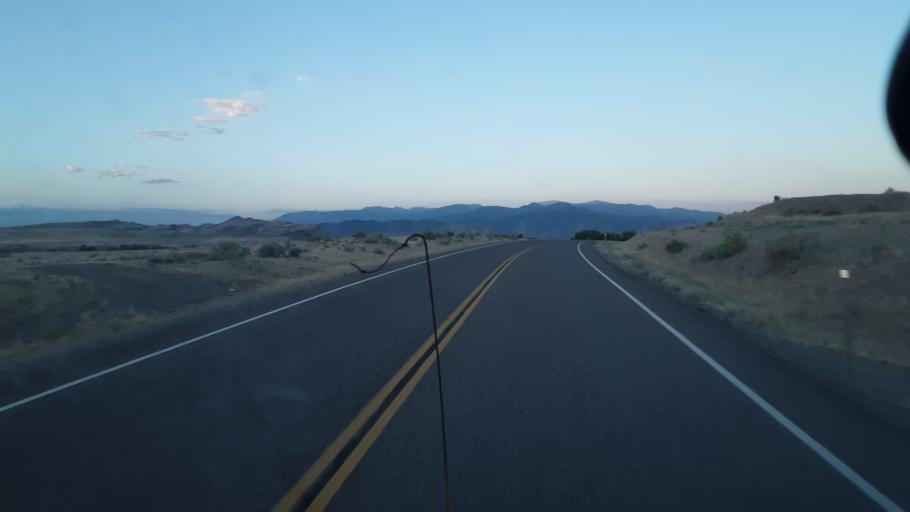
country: US
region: Utah
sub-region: Sevier County
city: Monroe
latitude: 38.6602
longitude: -112.1764
